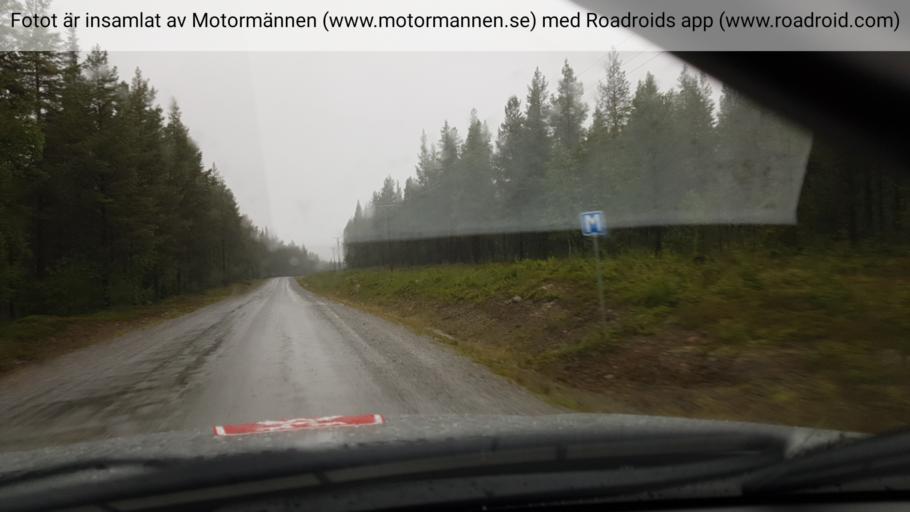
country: SE
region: Norrbotten
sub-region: Jokkmokks Kommun
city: Jokkmokk
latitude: 66.6219
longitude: 18.9204
